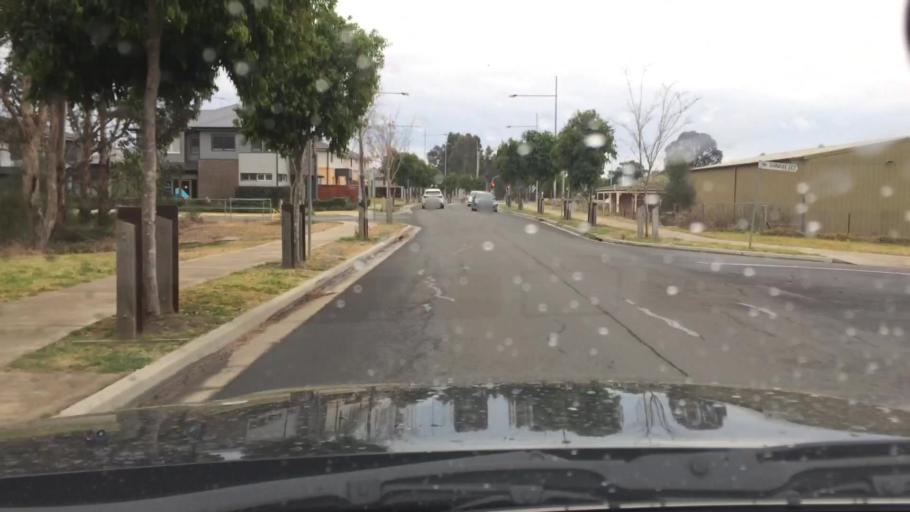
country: AU
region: New South Wales
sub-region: Campbelltown Municipality
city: Denham Court
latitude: -33.9526
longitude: 150.8451
